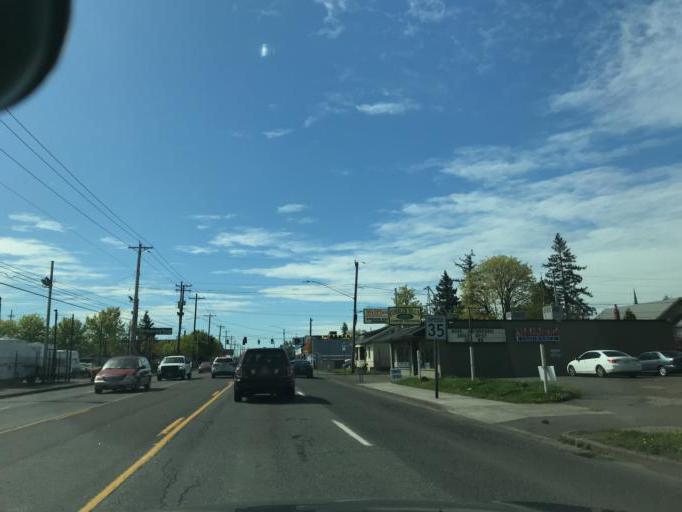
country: US
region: Oregon
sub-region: Multnomah County
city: Lents
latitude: 45.4808
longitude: -122.5790
